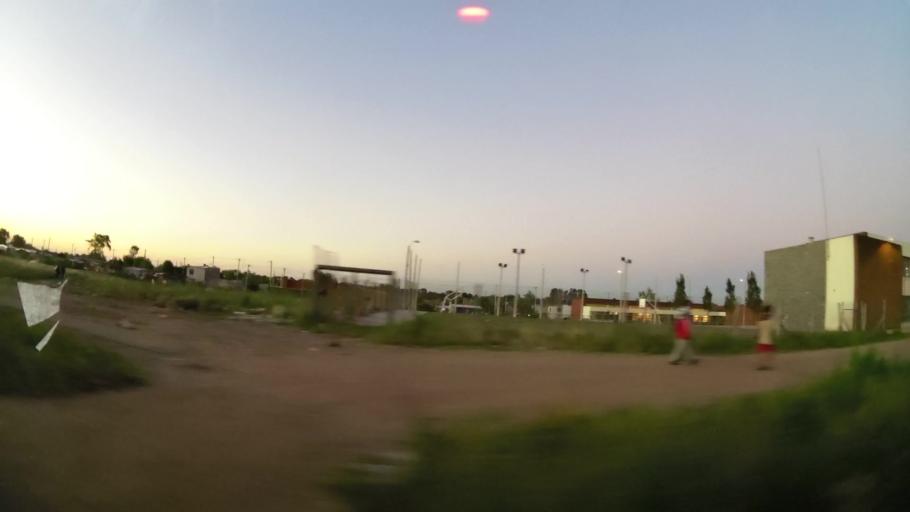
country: UY
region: Montevideo
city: Montevideo
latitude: -34.8226
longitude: -56.1619
